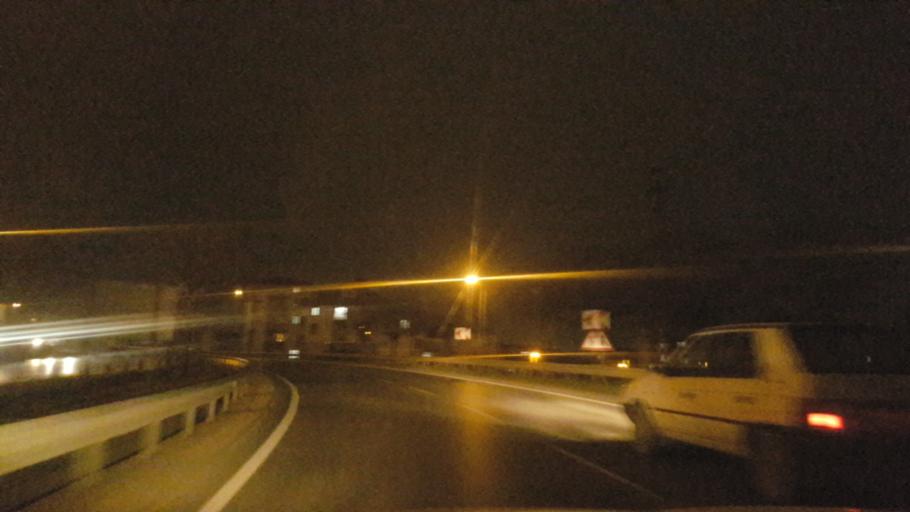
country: TR
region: Kocaeli
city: Darica
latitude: 40.7886
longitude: 29.4108
